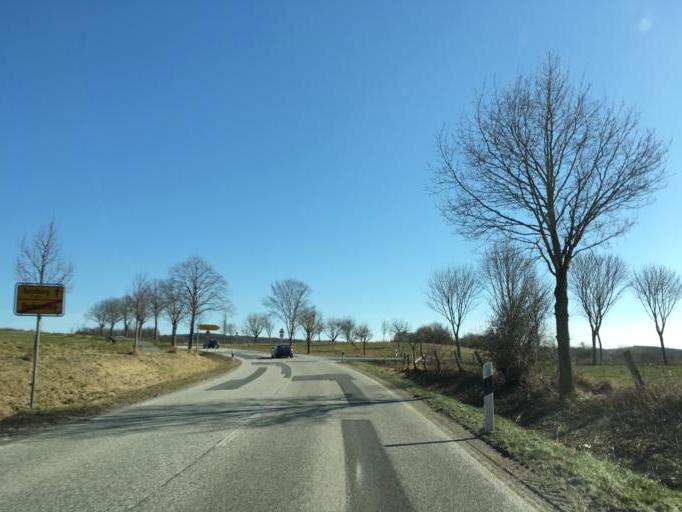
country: DE
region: Schleswig-Holstein
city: Berkenthin
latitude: 53.7301
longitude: 10.6528
